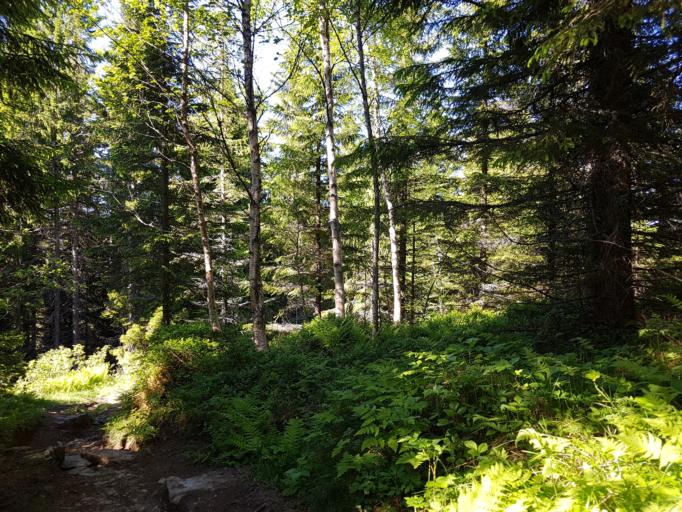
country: NO
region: Sor-Trondelag
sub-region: Trondheim
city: Trondheim
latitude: 63.4141
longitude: 10.3111
